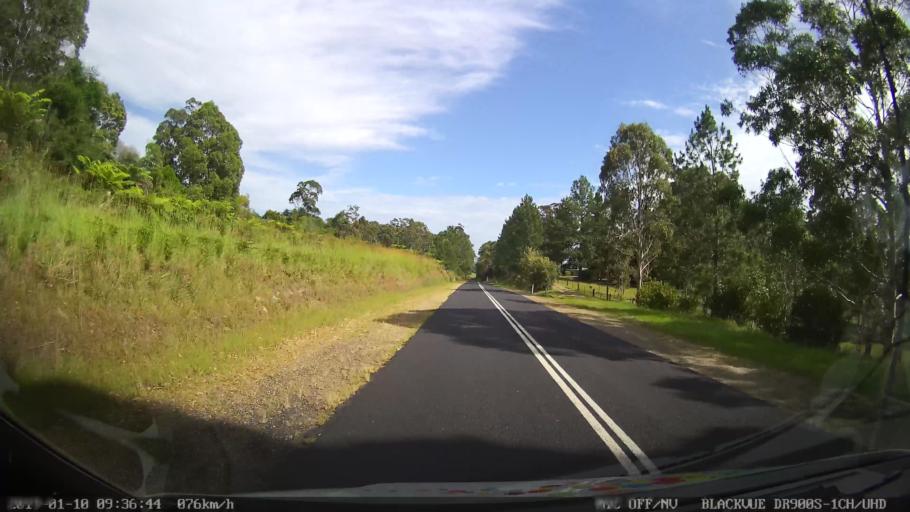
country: AU
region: New South Wales
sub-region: Coffs Harbour
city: Nana Glen
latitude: -30.1957
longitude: 153.0133
